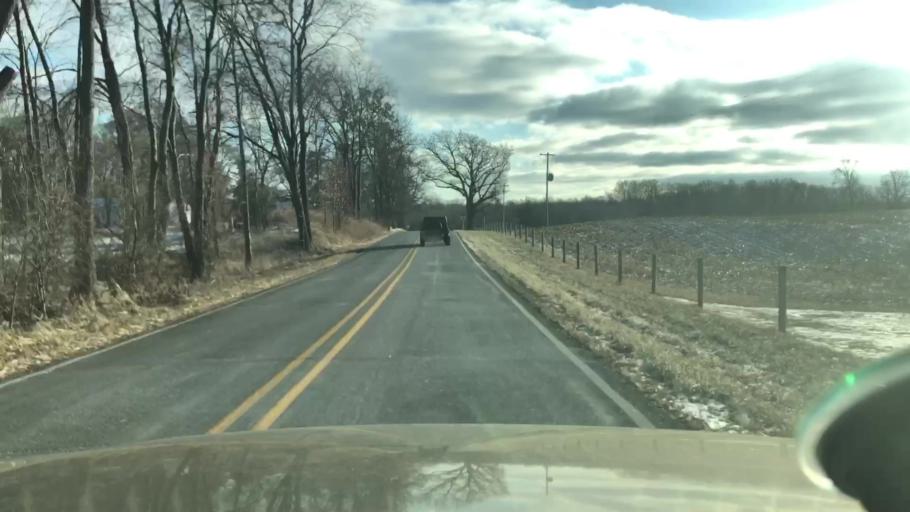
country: US
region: Michigan
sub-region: Jackson County
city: Vandercook Lake
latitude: 42.1001
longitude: -84.4511
